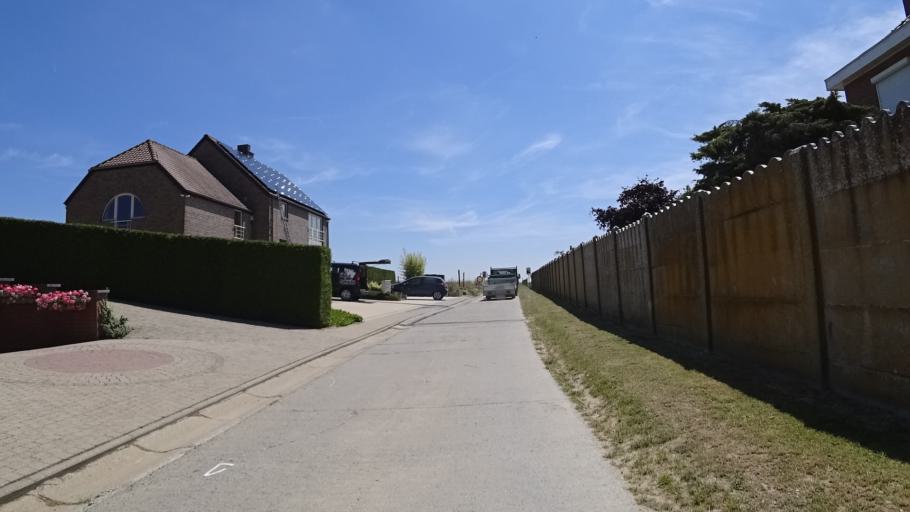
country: BE
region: Wallonia
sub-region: Province du Brabant Wallon
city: Chastre-Villeroux-Blanmont
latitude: 50.6073
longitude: 4.6607
